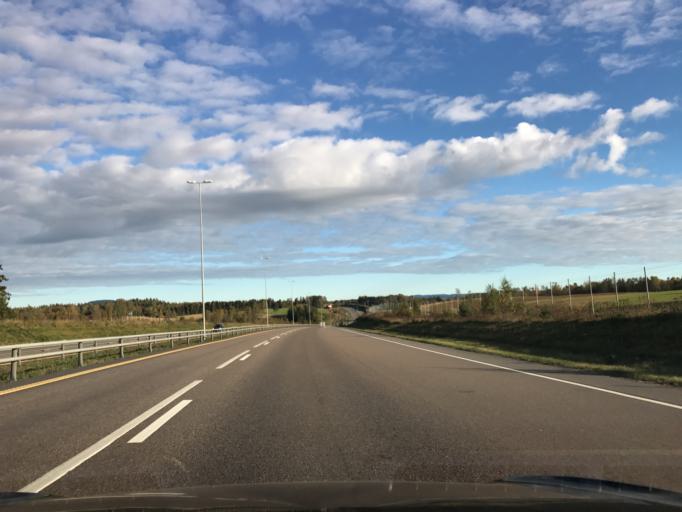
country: NO
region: Akershus
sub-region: Eidsvoll
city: Raholt
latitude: 60.2339
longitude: 11.1740
